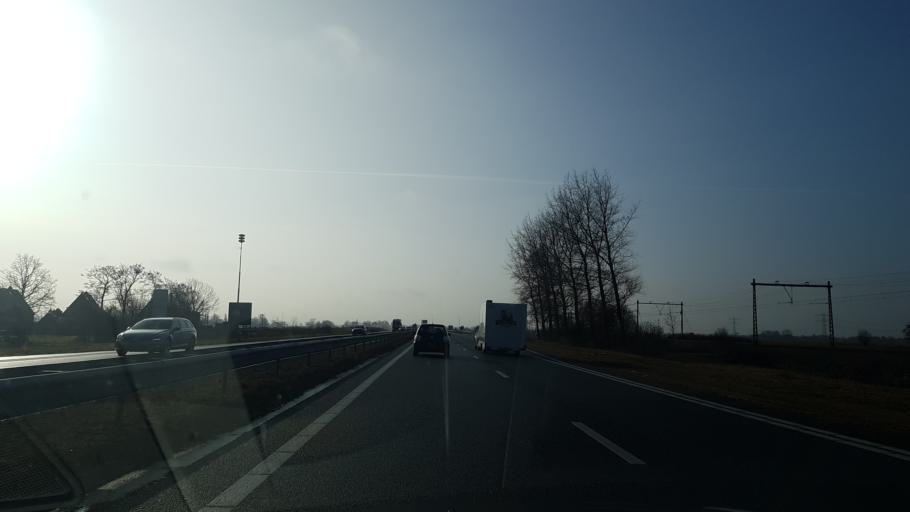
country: NL
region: Friesland
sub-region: Gemeente Leeuwarden
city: Wirdum
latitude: 53.1487
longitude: 5.7939
